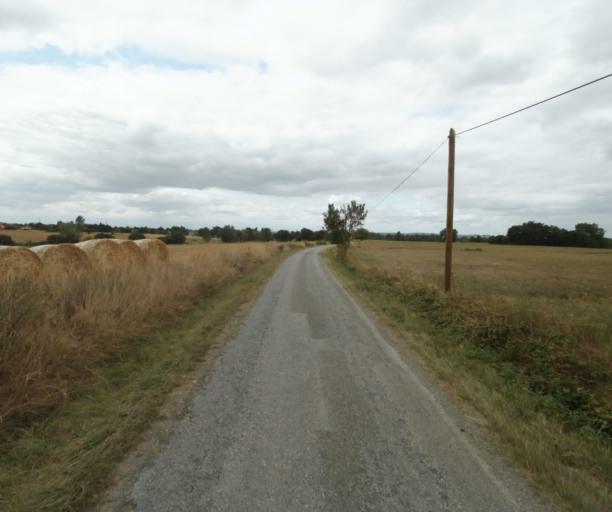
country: FR
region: Midi-Pyrenees
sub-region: Departement de la Haute-Garonne
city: Revel
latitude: 43.4805
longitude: 2.0305
